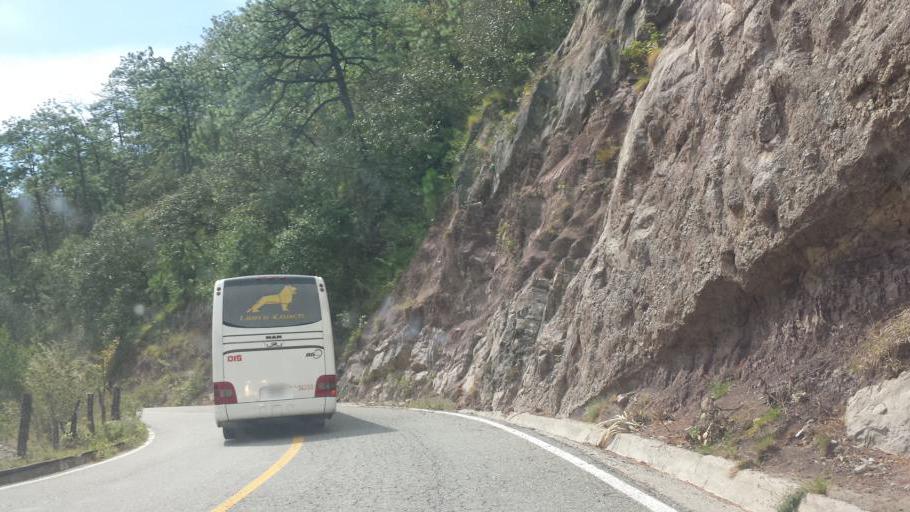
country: MX
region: Oaxaca
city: San Francisco Sola
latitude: 16.4506
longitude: -97.0329
